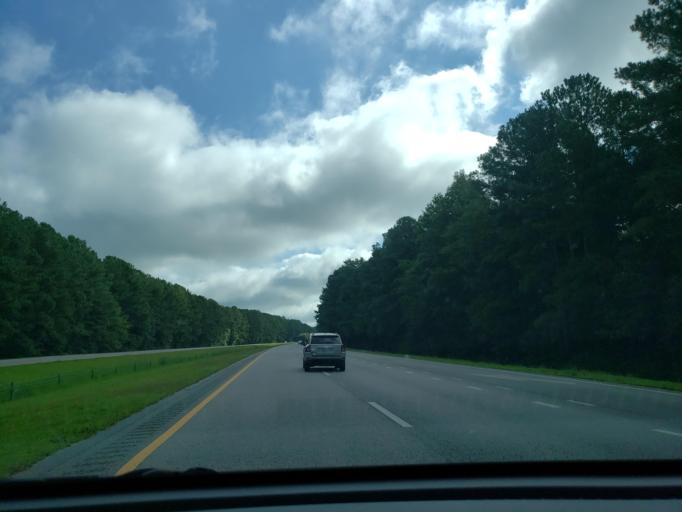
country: US
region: North Carolina
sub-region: Nash County
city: Spring Hope
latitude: 35.9426
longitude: -78.0483
